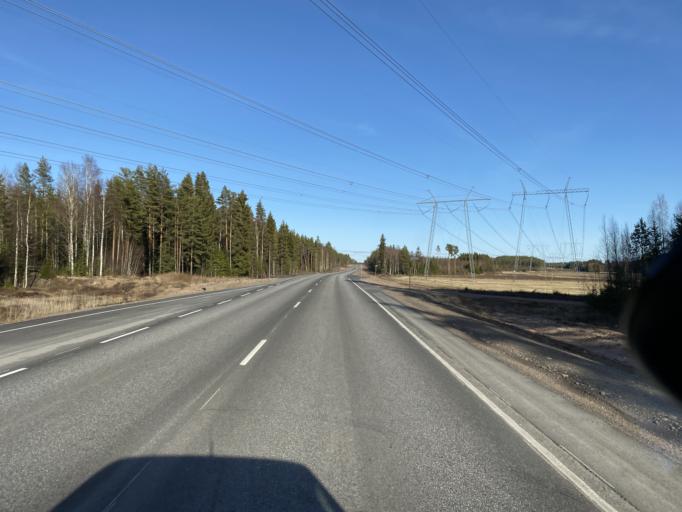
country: FI
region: Satakunta
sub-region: Rauma
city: Koeylioe
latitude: 61.1649
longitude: 22.3624
